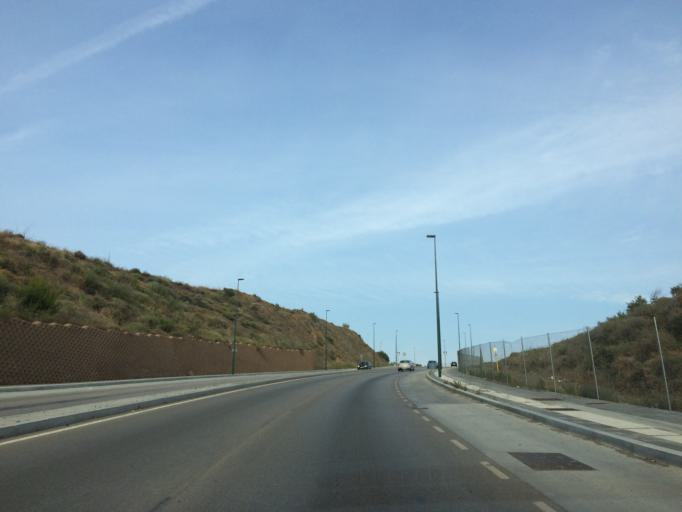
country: ES
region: Andalusia
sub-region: Provincia de Malaga
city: Malaga
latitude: 36.7369
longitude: -4.3994
